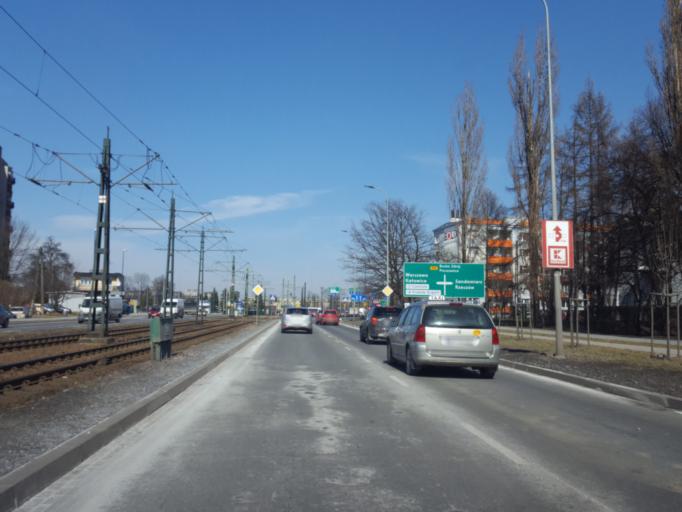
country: PL
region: Lesser Poland Voivodeship
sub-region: Krakow
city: Krakow
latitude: 50.0713
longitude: 20.0164
